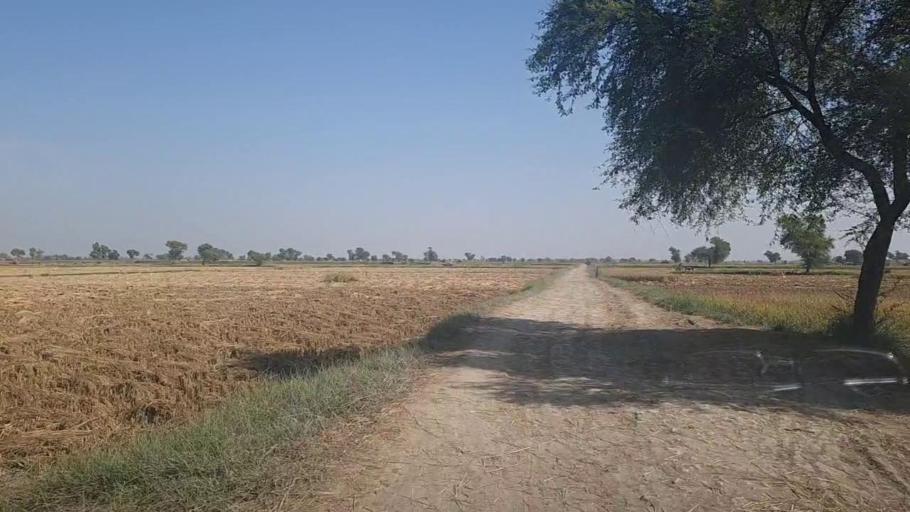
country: PK
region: Sindh
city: Thul
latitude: 28.2483
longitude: 68.8180
